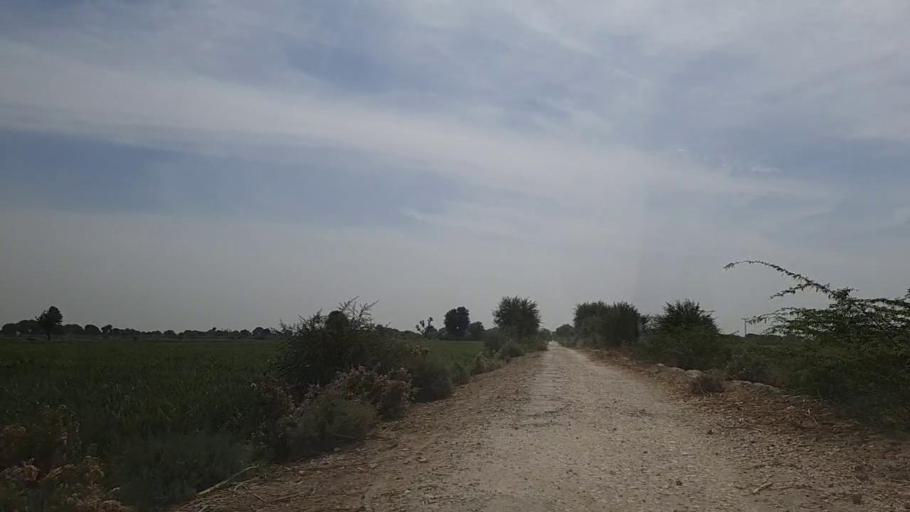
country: PK
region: Sindh
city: Samaro
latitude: 25.2701
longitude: 69.4536
